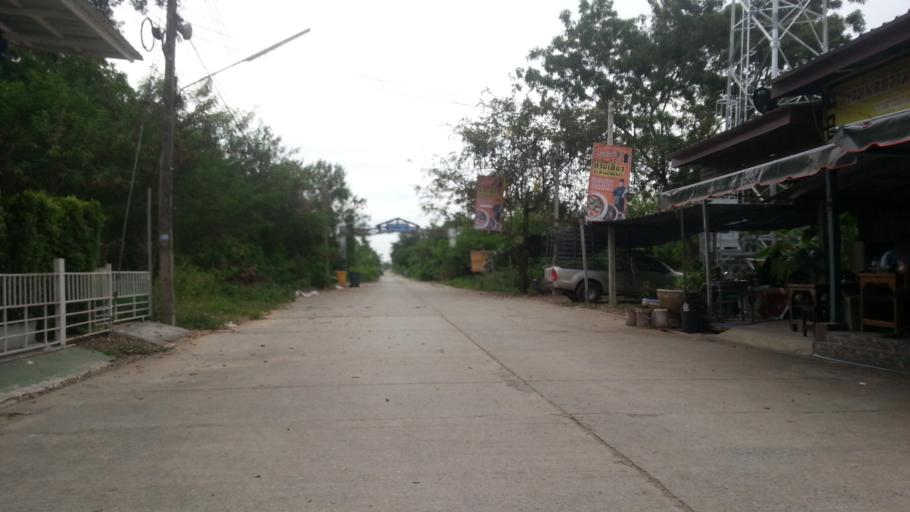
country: TH
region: Pathum Thani
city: Nong Suea
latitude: 14.0676
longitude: 100.8705
